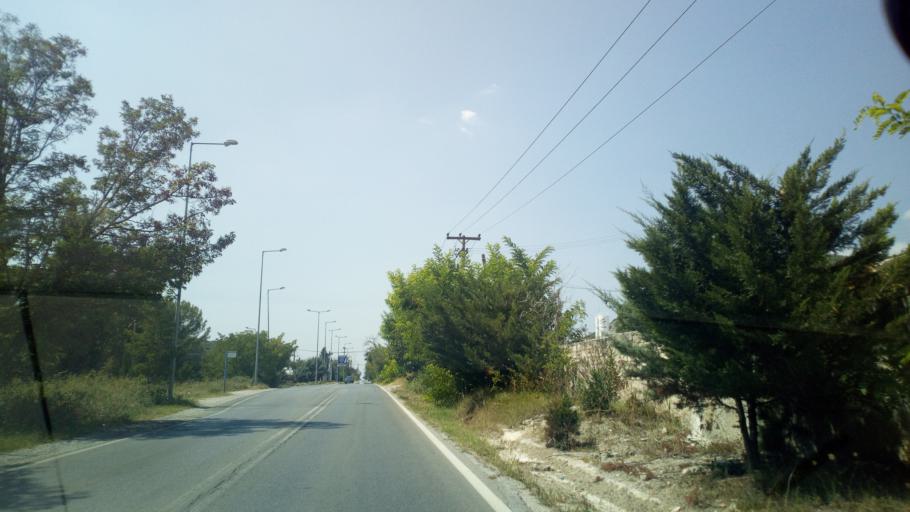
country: GR
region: Central Macedonia
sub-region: Nomos Thessalonikis
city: Chortiatis
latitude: 40.6254
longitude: 23.0662
